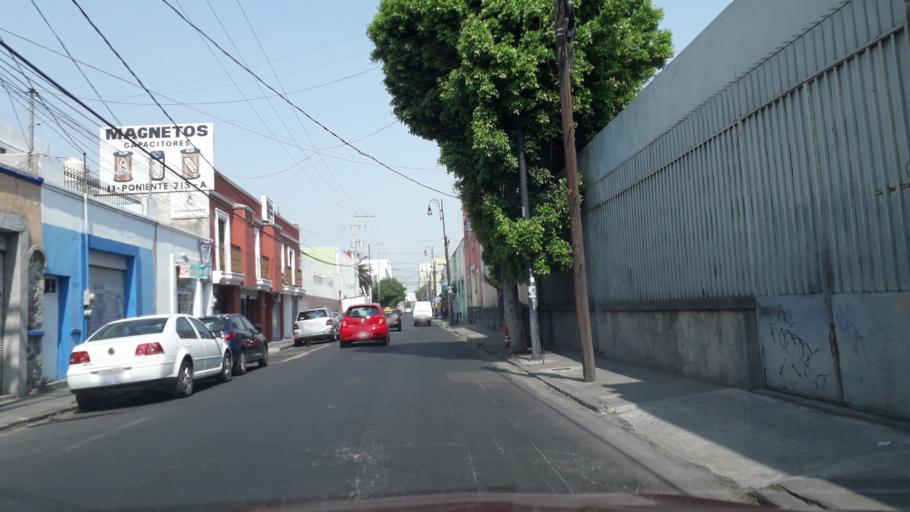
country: MX
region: Puebla
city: Puebla
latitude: 19.0433
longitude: -98.2061
